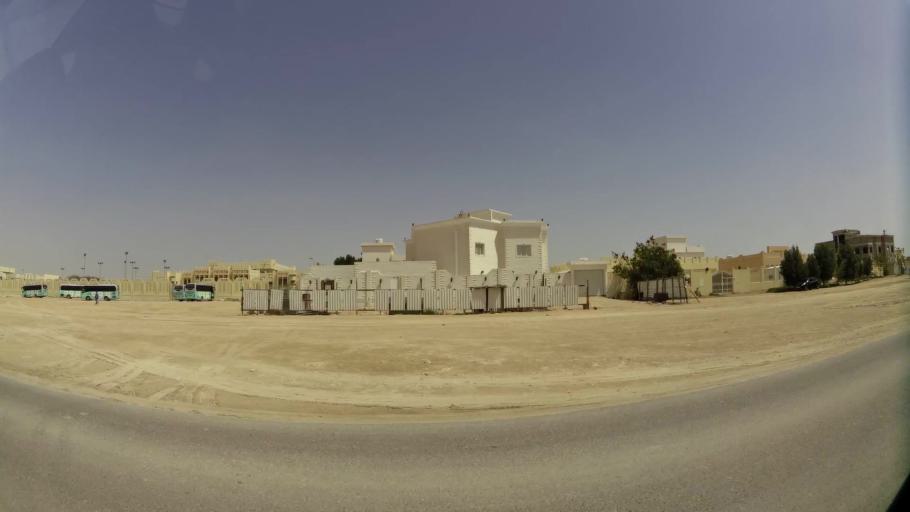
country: QA
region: Baladiyat Umm Salal
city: Umm Salal Muhammad
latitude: 25.3936
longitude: 51.4459
